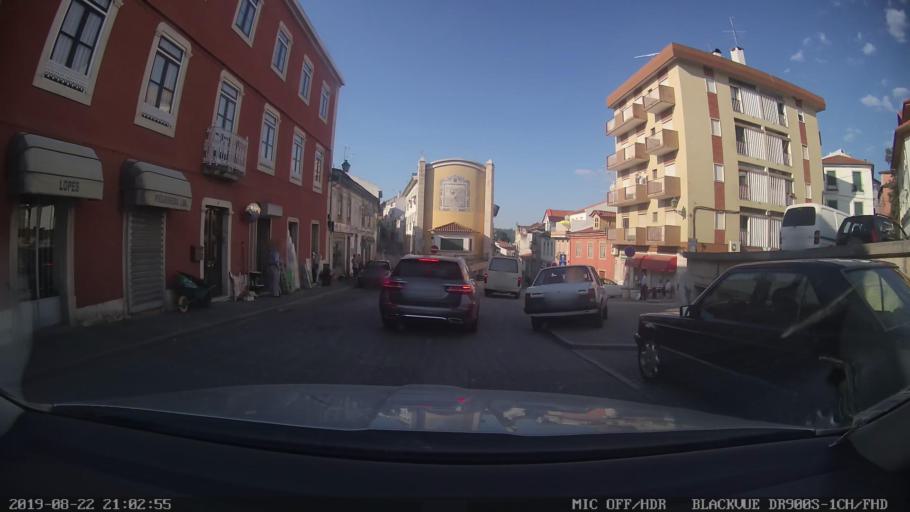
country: PT
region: Castelo Branco
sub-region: Serta
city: Serta
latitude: 39.8074
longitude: -8.0977
